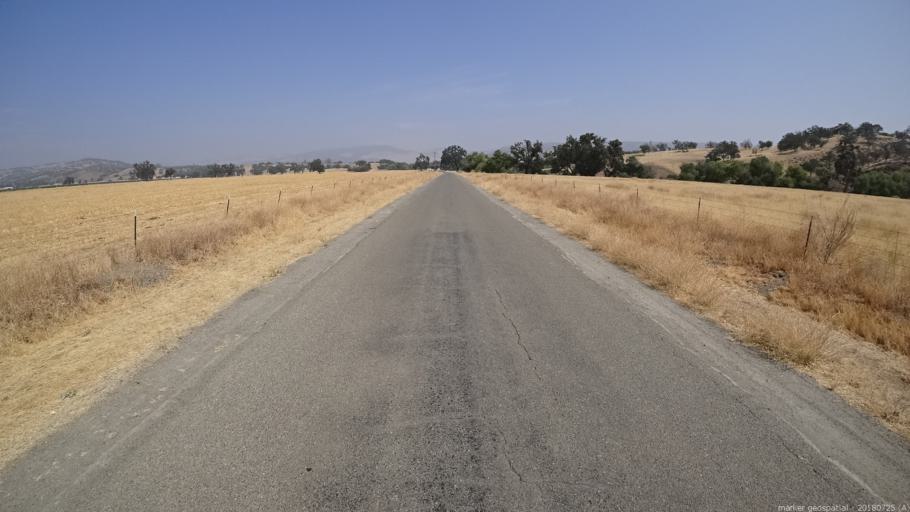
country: US
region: California
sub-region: San Luis Obispo County
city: Shandon
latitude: 35.8902
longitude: -120.4364
